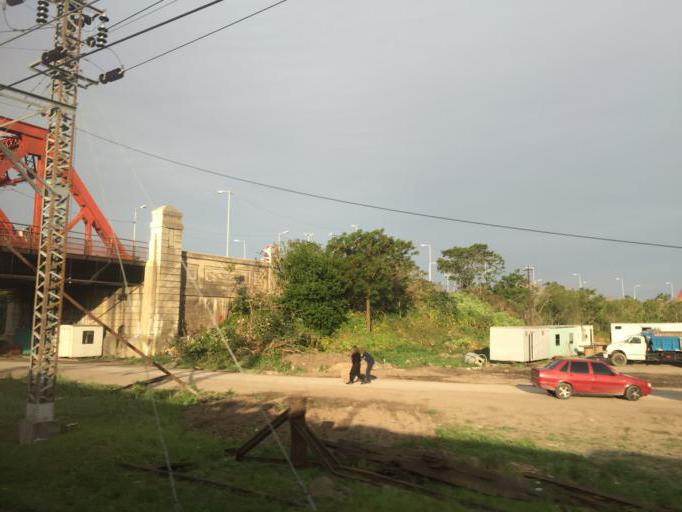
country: AR
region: Buenos Aires
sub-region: Partido de Avellaneda
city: Avellaneda
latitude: -34.6721
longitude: -58.3777
